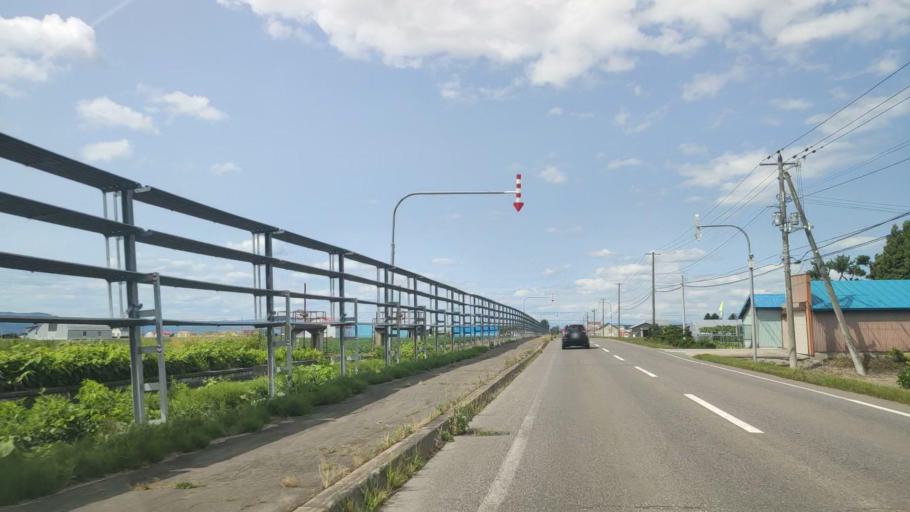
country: JP
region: Hokkaido
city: Nayoro
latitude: 44.1933
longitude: 142.4159
